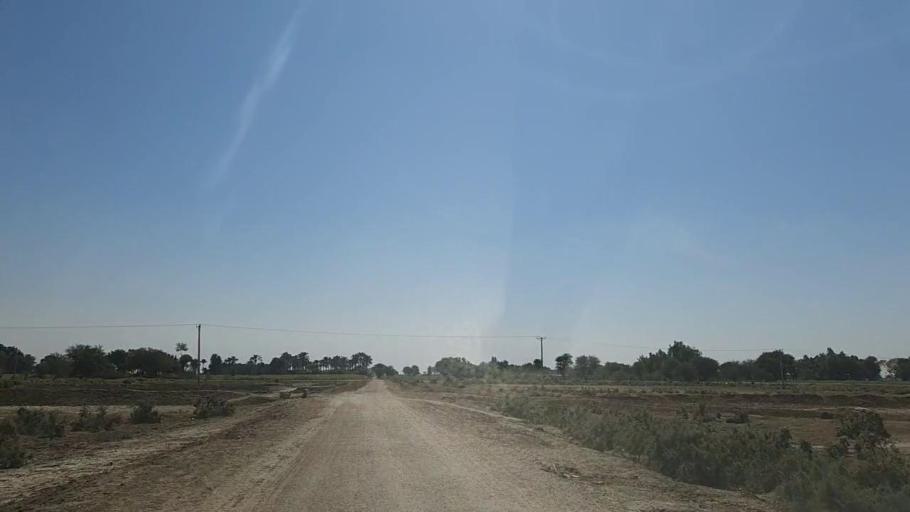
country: PK
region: Sindh
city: Samaro
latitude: 25.2945
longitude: 69.5027
